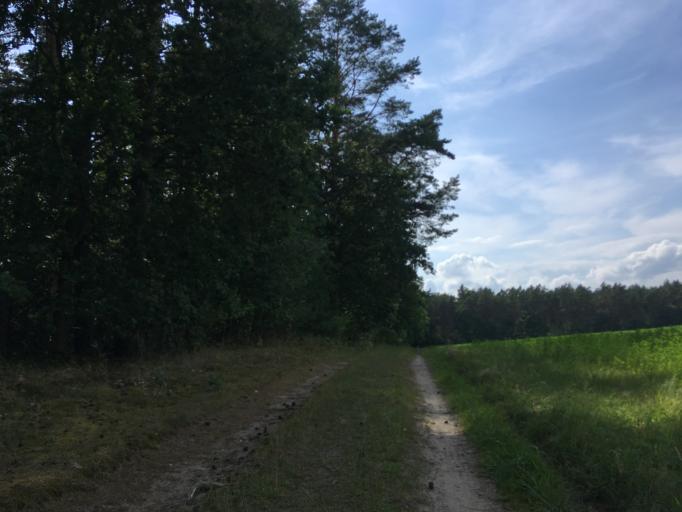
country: DE
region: Brandenburg
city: Rudnitz
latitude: 52.7466
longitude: 13.5803
